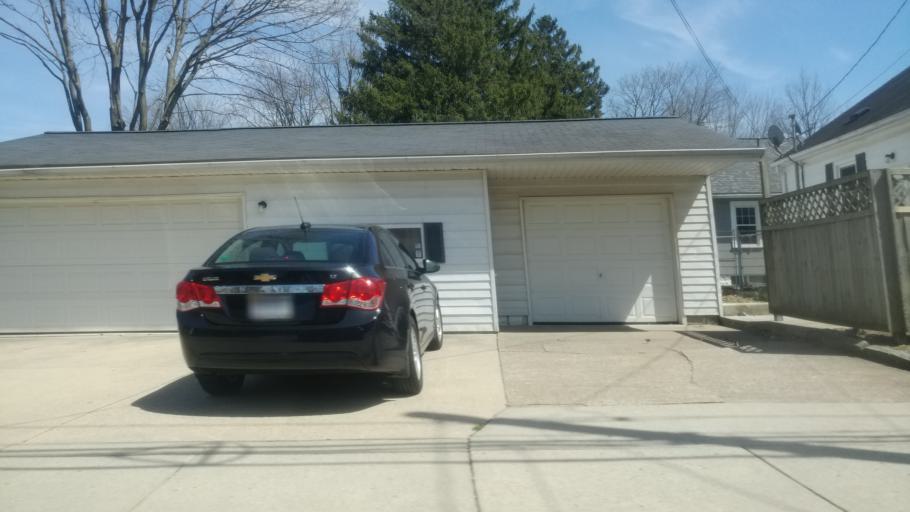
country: US
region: Ohio
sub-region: Wood County
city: Bowling Green
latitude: 41.3838
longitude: -83.6534
